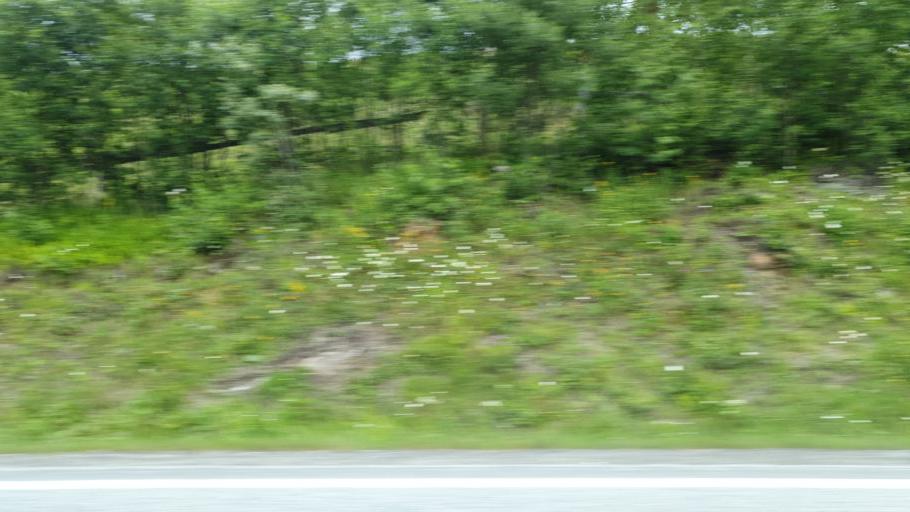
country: NO
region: Sor-Trondelag
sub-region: Rennebu
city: Berkak
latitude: 62.8774
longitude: 10.0889
